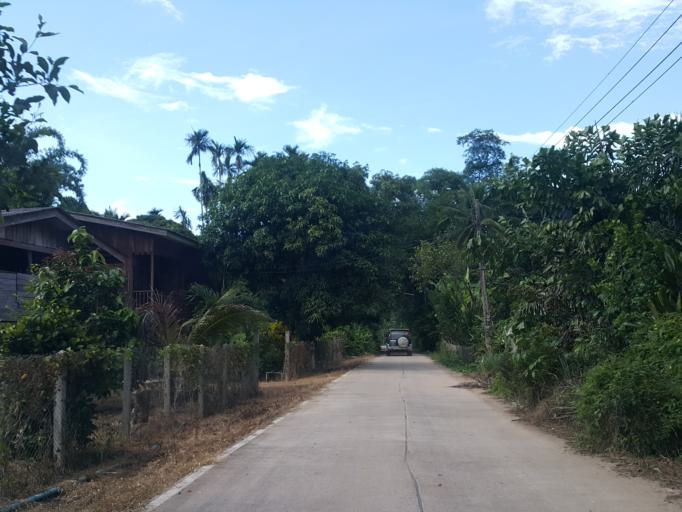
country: TH
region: Chiang Mai
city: Phrao
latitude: 19.3406
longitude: 99.1845
